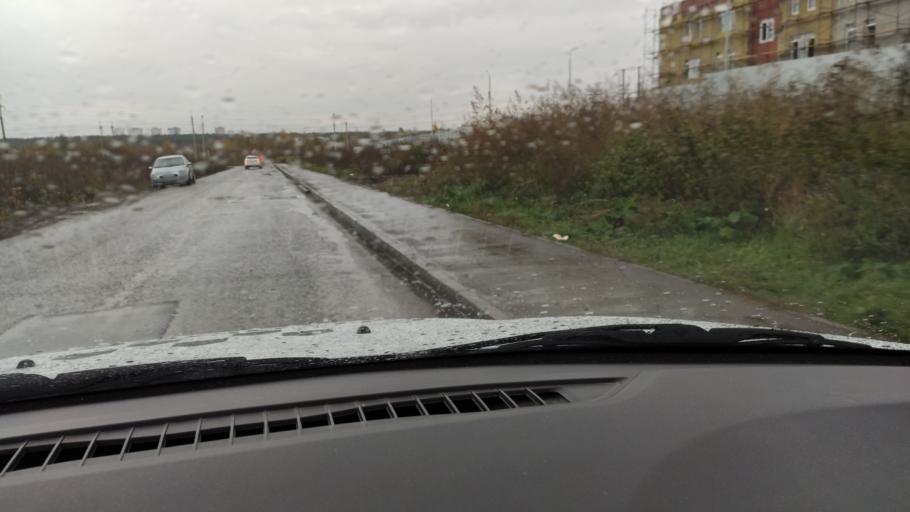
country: RU
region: Perm
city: Kondratovo
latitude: 57.9867
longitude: 56.1192
